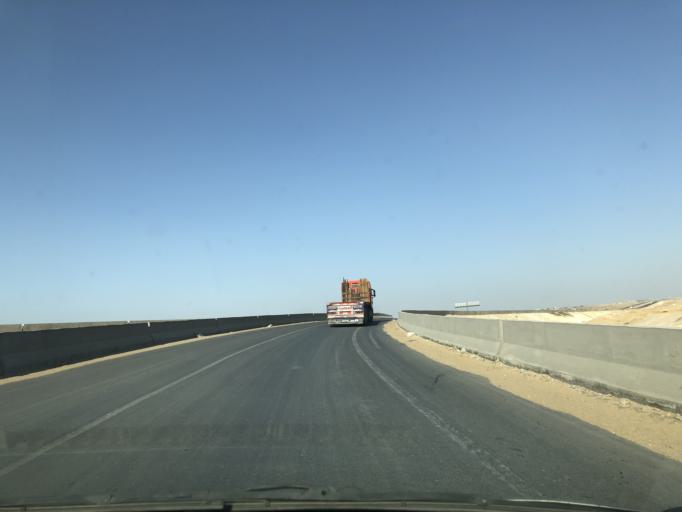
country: EG
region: Muhafazat al Minufiyah
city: Ashmun
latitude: 30.0667
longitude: 30.8466
